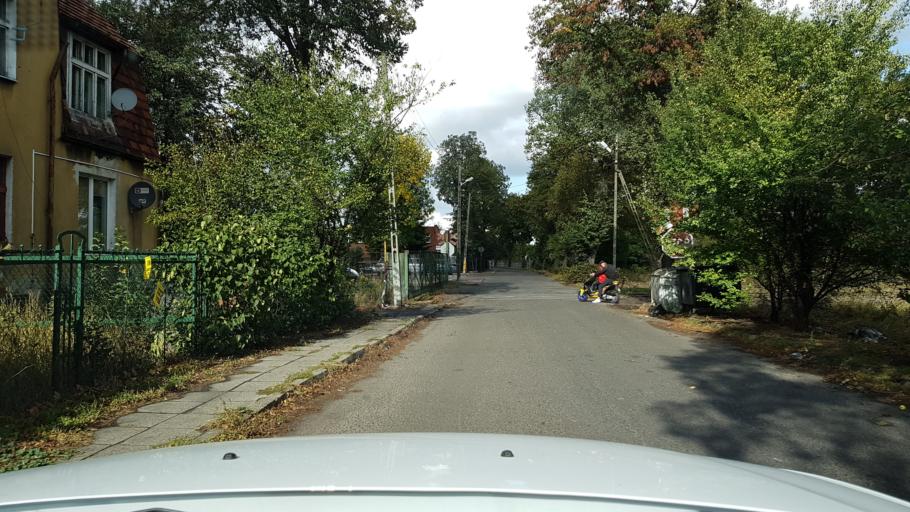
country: PL
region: West Pomeranian Voivodeship
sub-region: Powiat gryfinski
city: Gryfino
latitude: 53.2819
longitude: 14.4990
